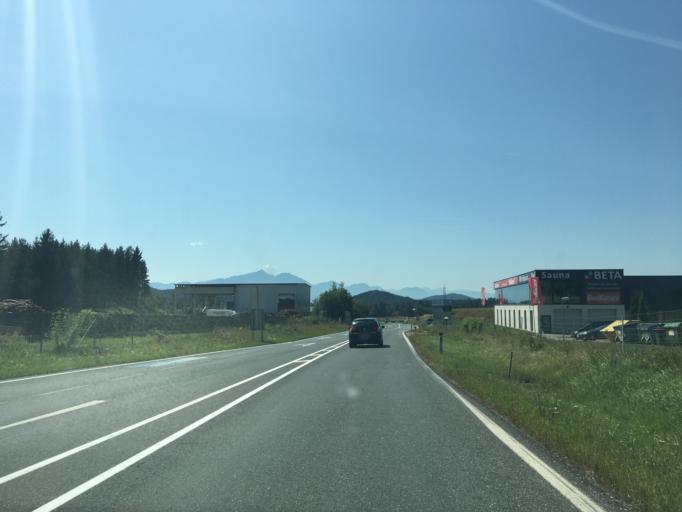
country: AT
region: Carinthia
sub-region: Politischer Bezirk Volkermarkt
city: Voelkermarkt
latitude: 46.6822
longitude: 14.6793
